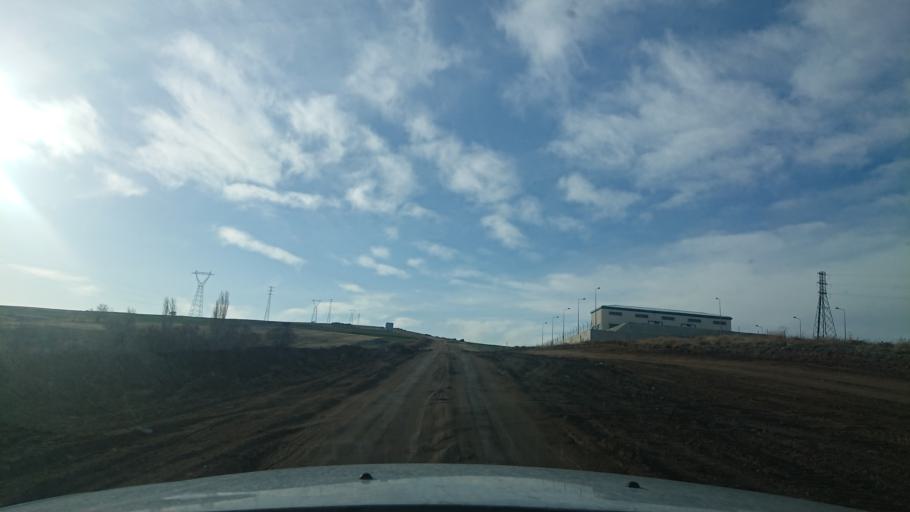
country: TR
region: Aksaray
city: Agacoren
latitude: 38.8545
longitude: 33.9430
